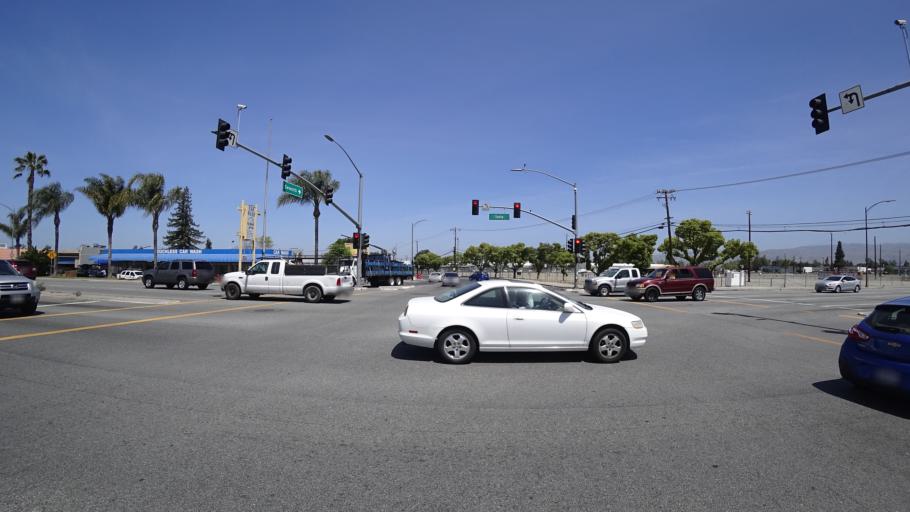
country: US
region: California
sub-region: Santa Clara County
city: Seven Trees
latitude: 37.3035
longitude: -121.8548
